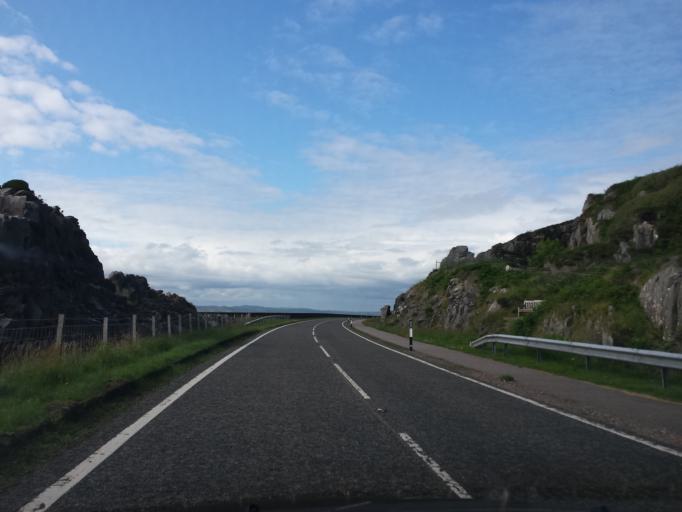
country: GB
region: Scotland
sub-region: Highland
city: Portree
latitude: 56.9991
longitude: -5.8336
